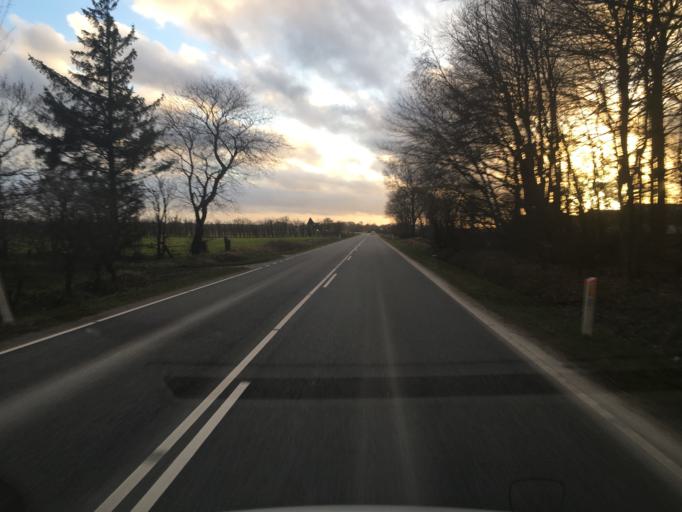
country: DK
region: South Denmark
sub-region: Aabenraa Kommune
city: Tinglev
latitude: 54.9645
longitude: 9.3007
